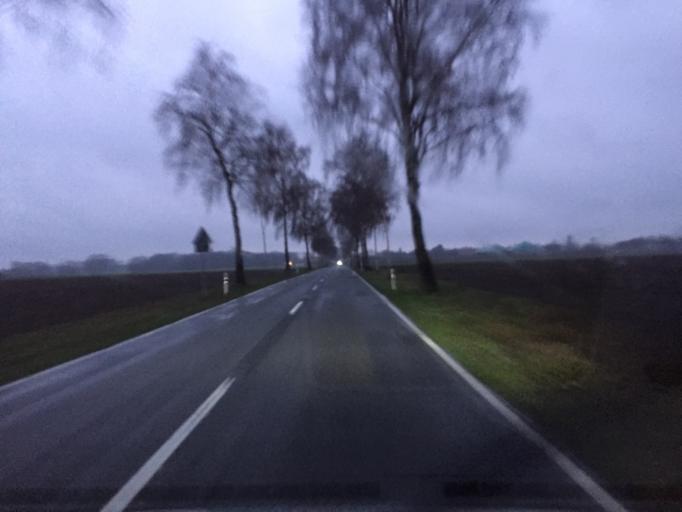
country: DE
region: Lower Saxony
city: Sudwalde
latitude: 52.8043
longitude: 8.8423
